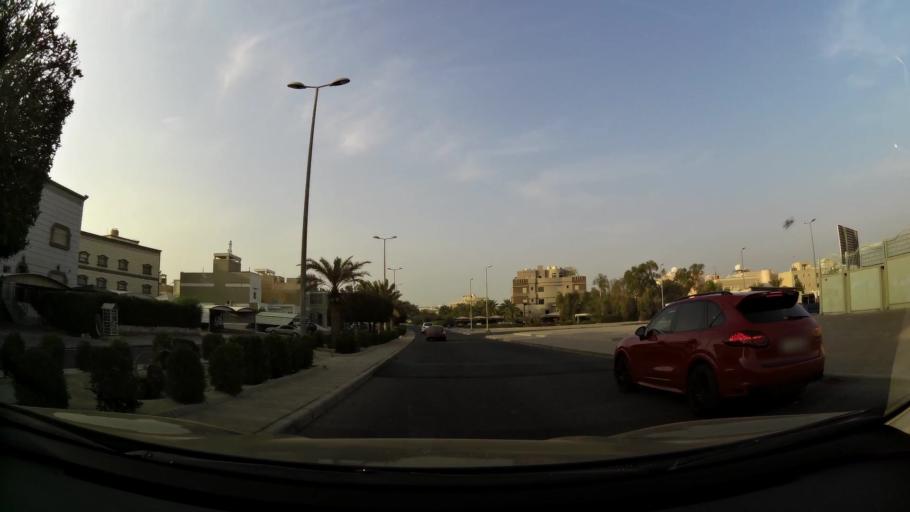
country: KW
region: Mubarak al Kabir
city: Sabah as Salim
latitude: 29.2529
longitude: 48.0712
